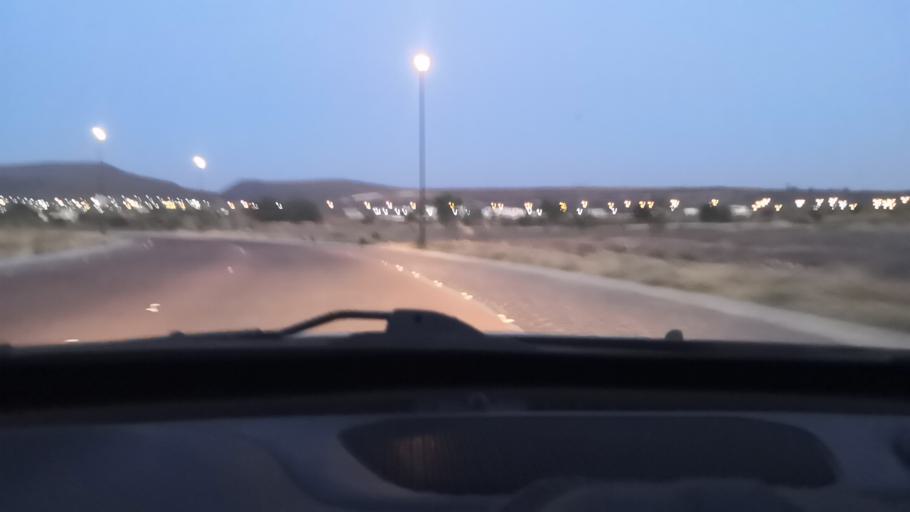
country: MX
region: Guanajuato
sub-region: Leon
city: Fraccionamiento Paseo de las Torres
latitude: 21.2316
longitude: -101.7989
